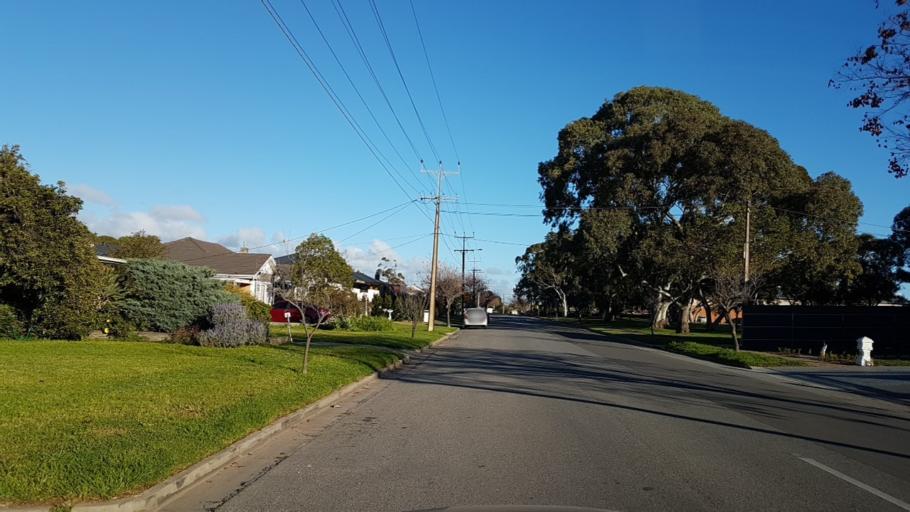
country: AU
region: South Australia
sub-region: Charles Sturt
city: Seaton
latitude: -34.9290
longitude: 138.5241
